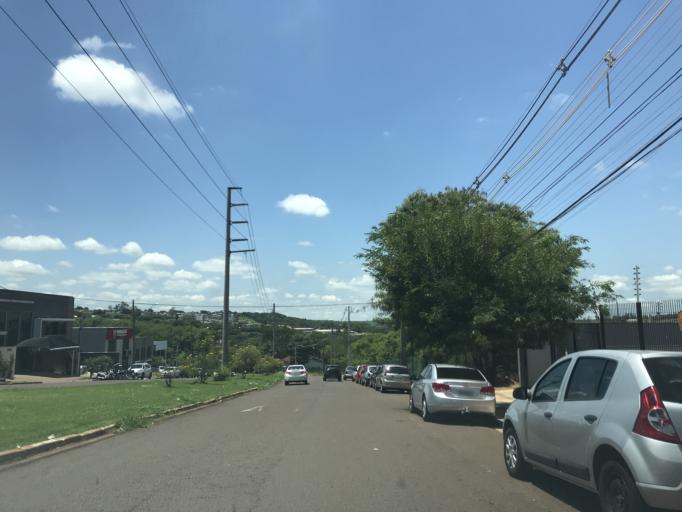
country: BR
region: Parana
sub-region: Maringa
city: Maringa
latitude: -23.4516
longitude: -51.9321
